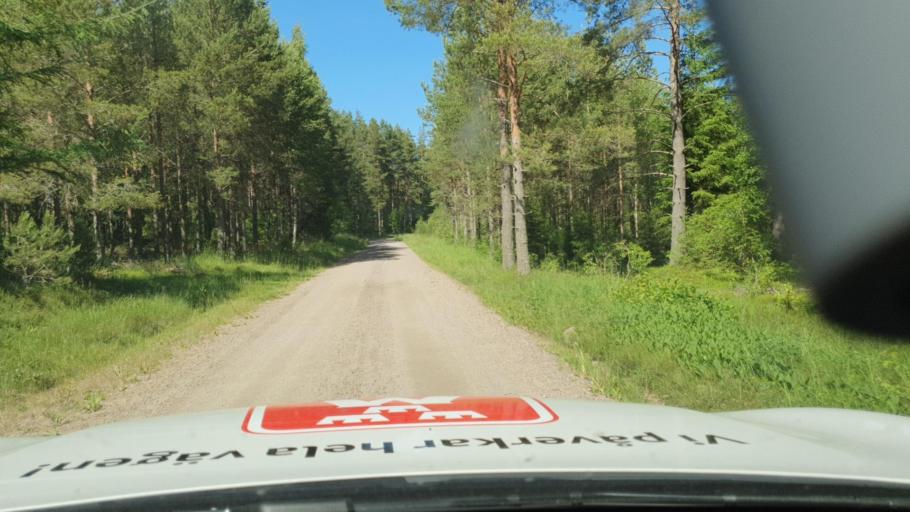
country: SE
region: Vaestra Goetaland
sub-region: Skovde Kommun
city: Skultorp
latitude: 58.3093
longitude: 13.8460
